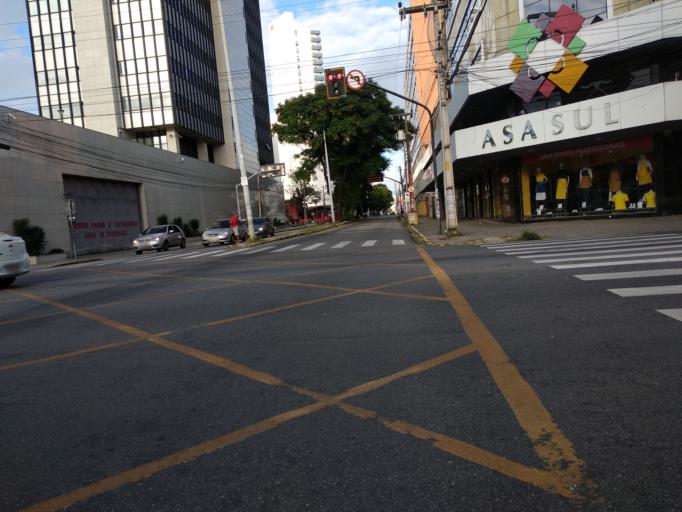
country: BR
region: Ceara
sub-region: Fortaleza
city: Fortaleza
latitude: -3.7339
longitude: -38.5233
